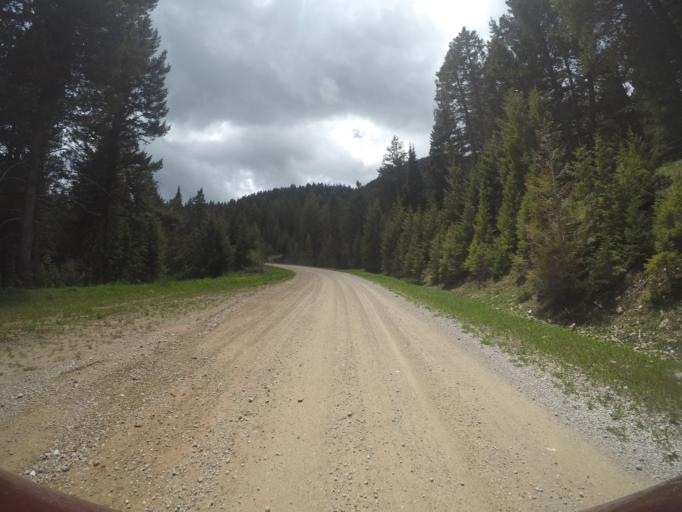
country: US
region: Wyoming
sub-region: Big Horn County
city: Lovell
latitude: 45.1833
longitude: -108.4706
